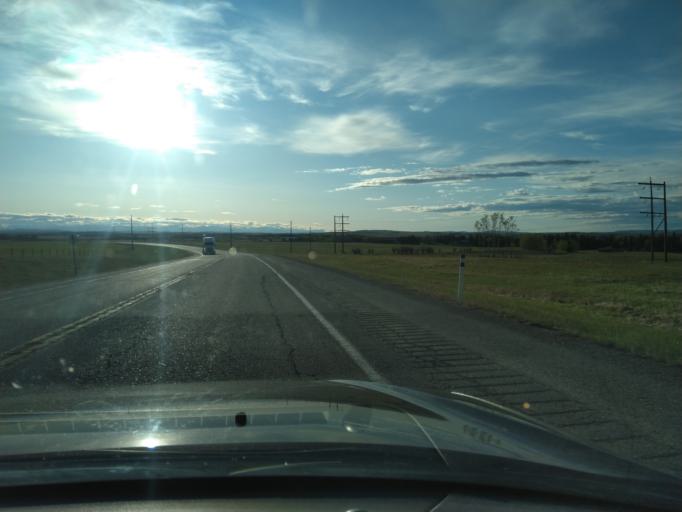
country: CA
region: Alberta
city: Cochrane
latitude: 51.0217
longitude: -114.3285
